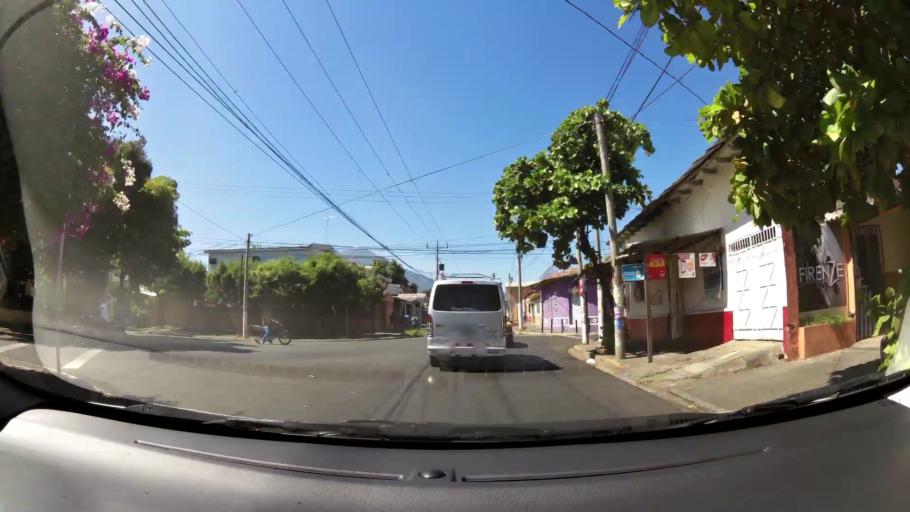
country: SV
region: San Miguel
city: San Miguel
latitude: 13.4784
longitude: -88.1705
